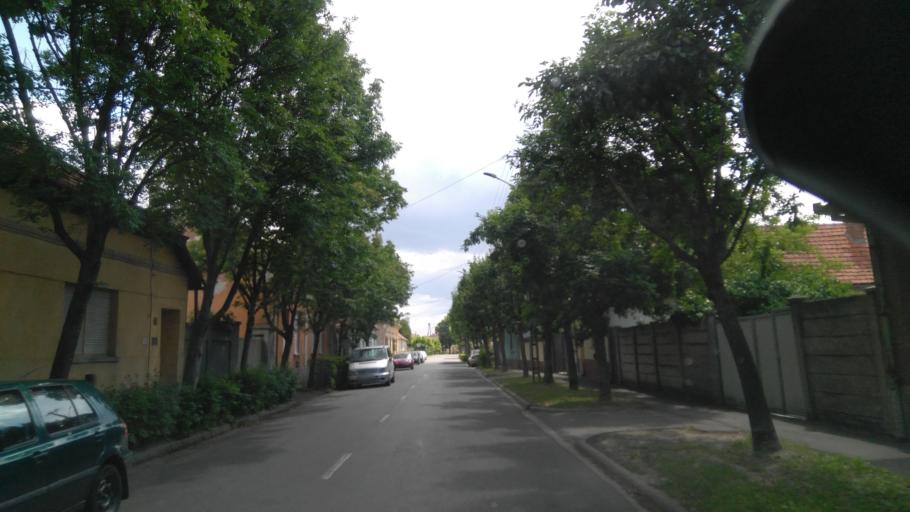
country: HU
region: Bekes
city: Gyula
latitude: 46.6457
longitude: 21.2617
